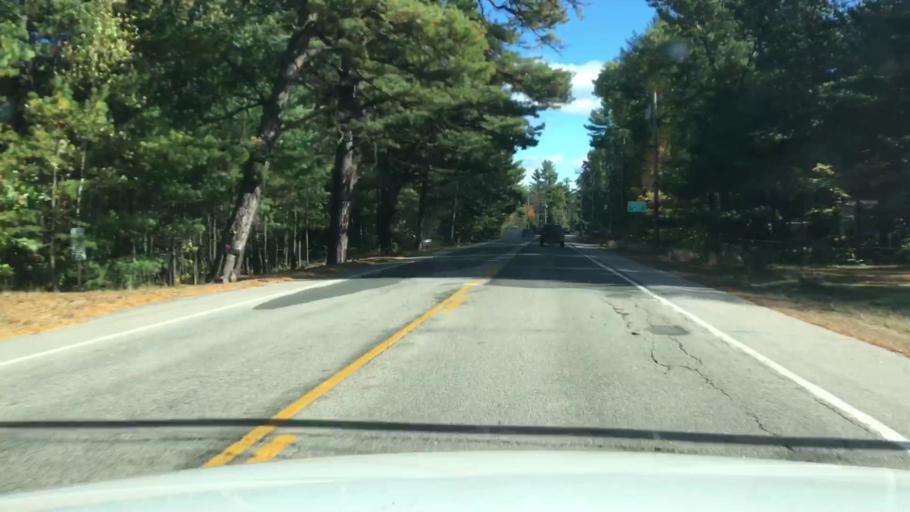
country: US
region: Maine
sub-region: York County
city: South Sanford
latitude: 43.3782
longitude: -70.6831
